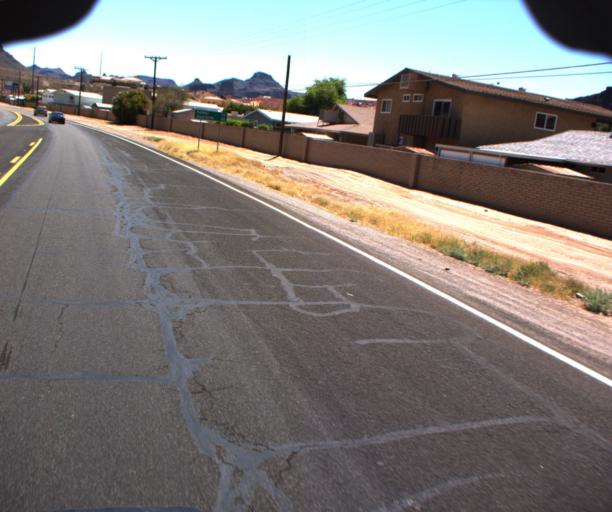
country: US
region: Arizona
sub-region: La Paz County
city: Cienega Springs
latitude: 34.2837
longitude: -114.1342
